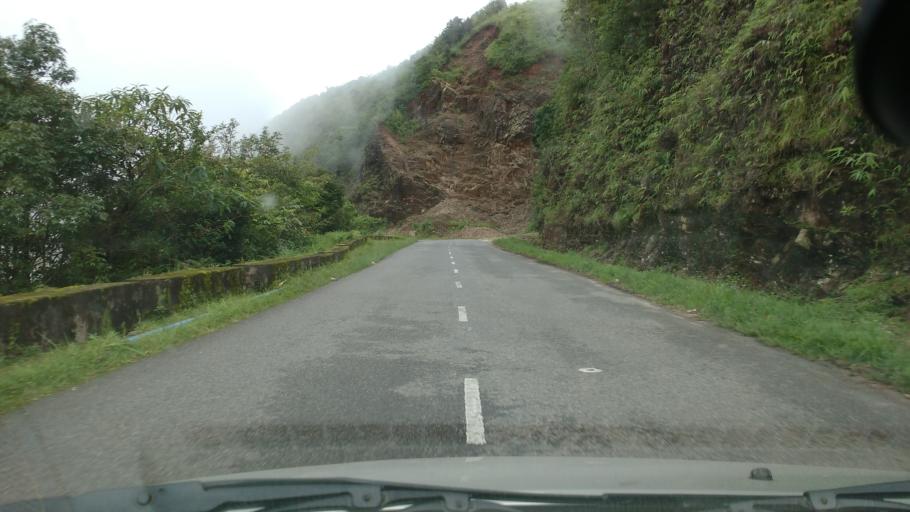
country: IN
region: Meghalaya
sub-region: East Khasi Hills
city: Cherrapunji
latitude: 25.3764
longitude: 91.8725
